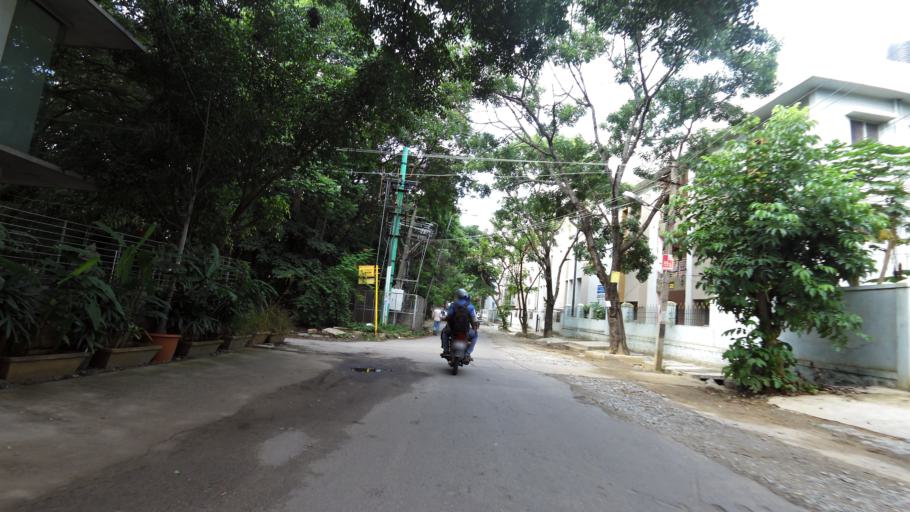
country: IN
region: Karnataka
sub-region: Bangalore Urban
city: Bangalore
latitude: 12.9808
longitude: 77.6337
